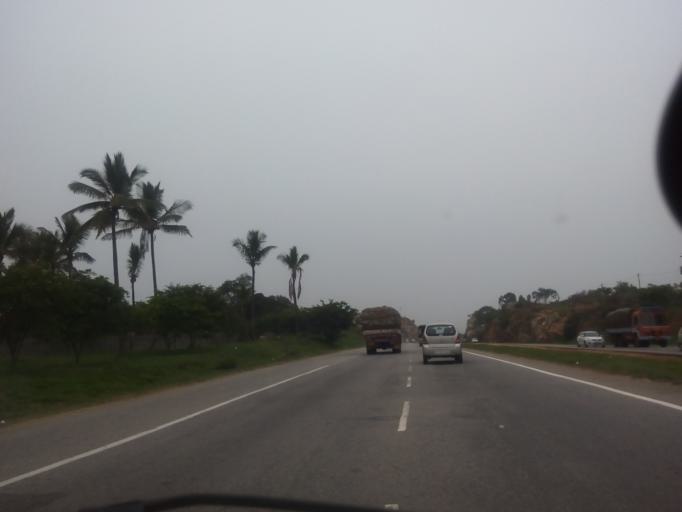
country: IN
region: Karnataka
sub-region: Bangalore Urban
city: Bangalore
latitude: 12.8500
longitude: 77.5774
